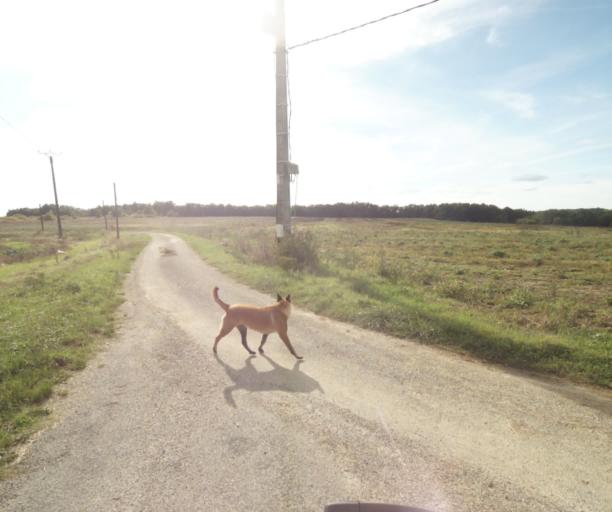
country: FR
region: Midi-Pyrenees
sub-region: Departement du Tarn-et-Garonne
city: Saint-Porquier
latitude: 43.9518
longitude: 1.1382
